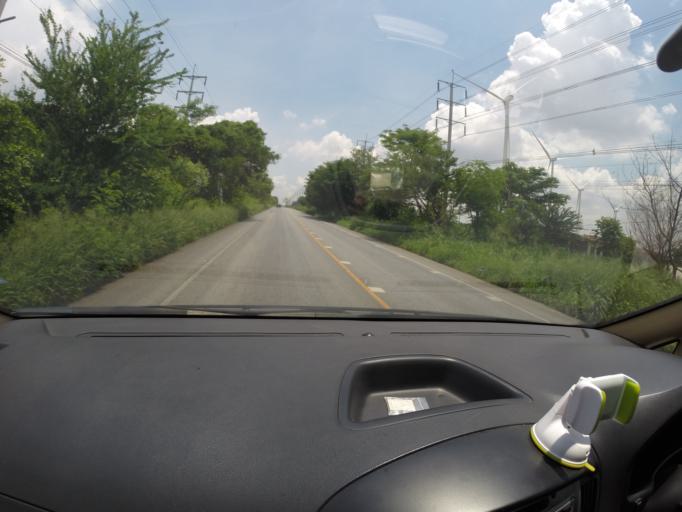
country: TH
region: Nakhon Ratchasima
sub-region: Amphoe Thepharak
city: Thepharak
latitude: 15.1191
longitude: 101.4871
